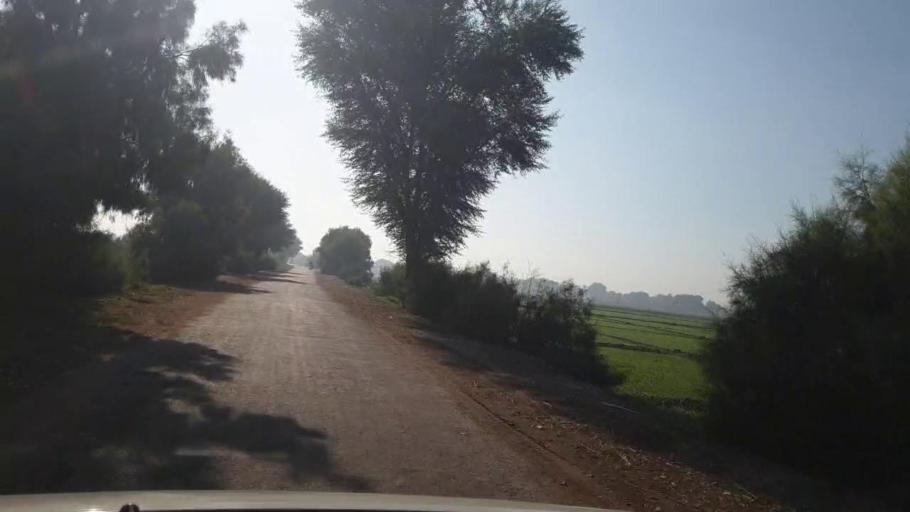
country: PK
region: Sindh
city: Dadu
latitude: 26.6618
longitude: 67.8191
